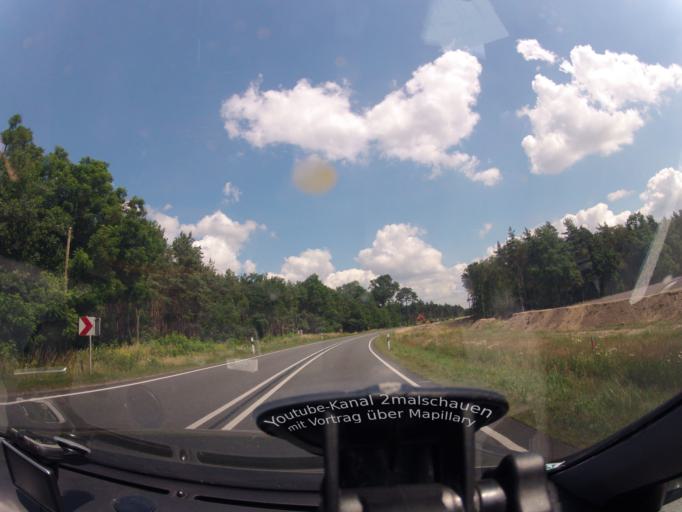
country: DE
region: Saxony
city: Mockrehna
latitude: 51.5245
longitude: 12.8653
